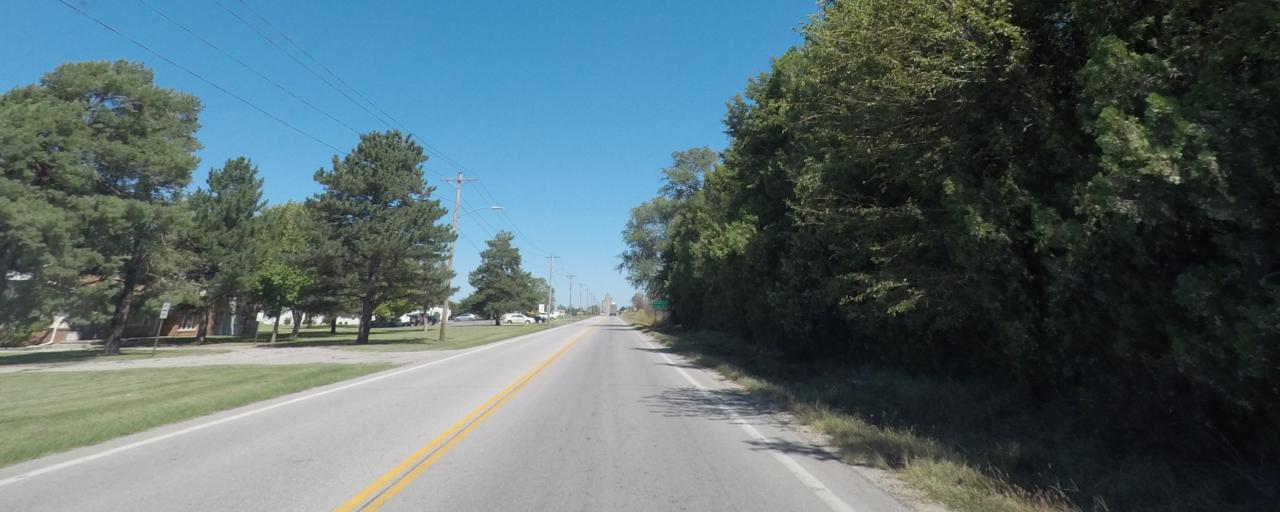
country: US
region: Kansas
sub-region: Sumner County
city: Wellington
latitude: 37.2900
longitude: -97.3943
